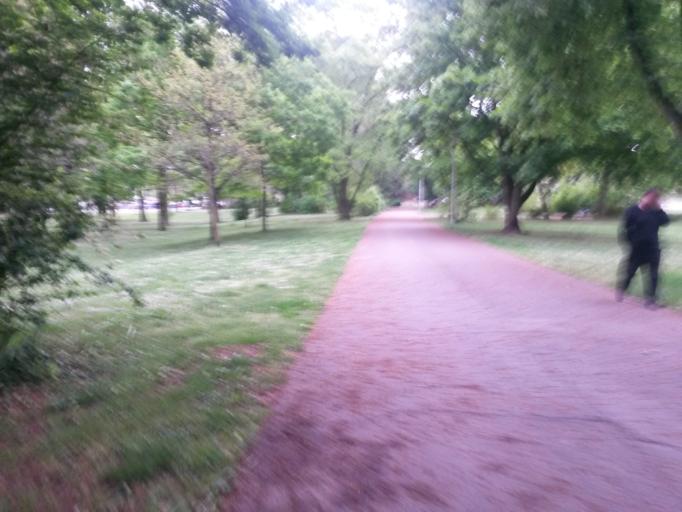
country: DE
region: Bavaria
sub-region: Regierungsbezirk Mittelfranken
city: Zirndorf
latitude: 49.4409
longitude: 10.9660
